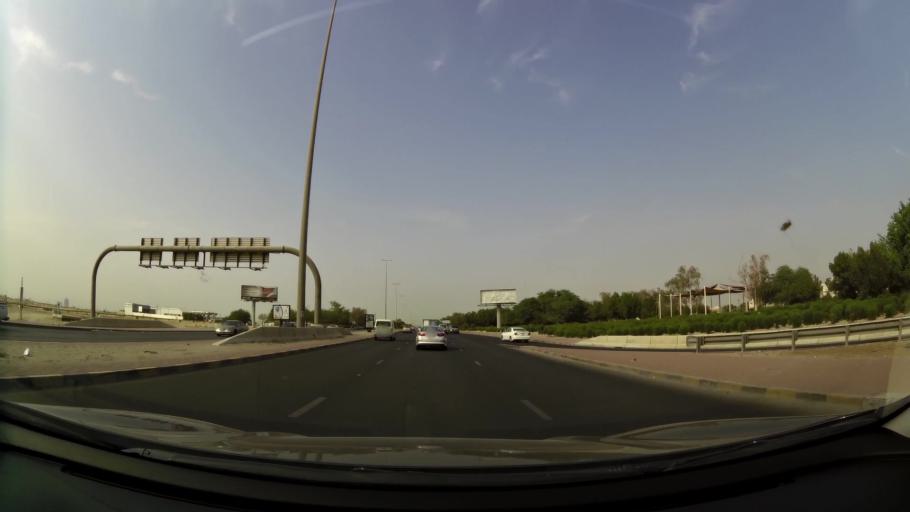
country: KW
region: Al Farwaniyah
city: Al Farwaniyah
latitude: 29.3049
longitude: 47.9633
